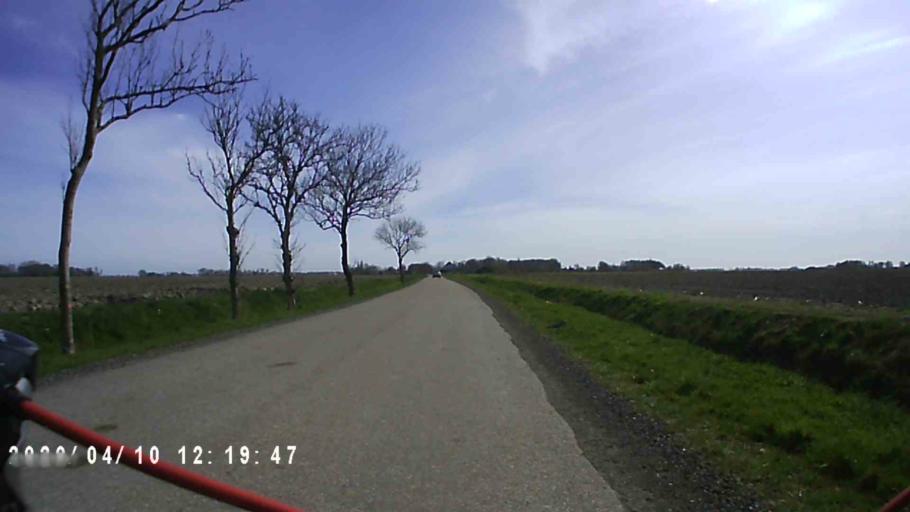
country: NL
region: Groningen
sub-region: Gemeente De Marne
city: Ulrum
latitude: 53.3958
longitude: 6.3948
